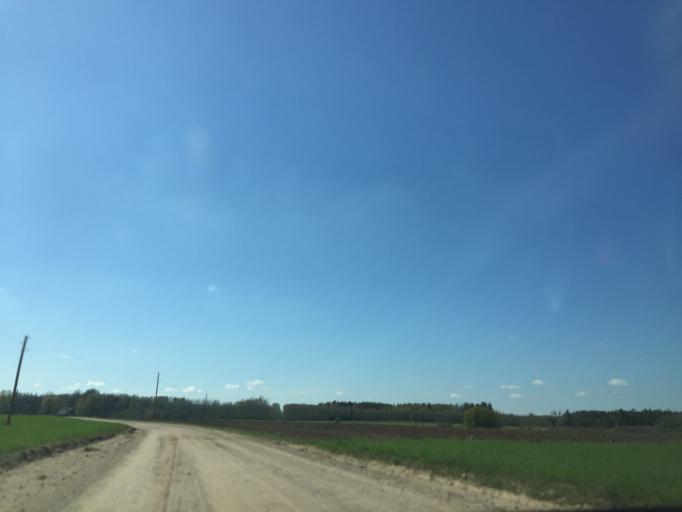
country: LV
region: Smiltene
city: Smiltene
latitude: 57.5582
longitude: 25.8882
